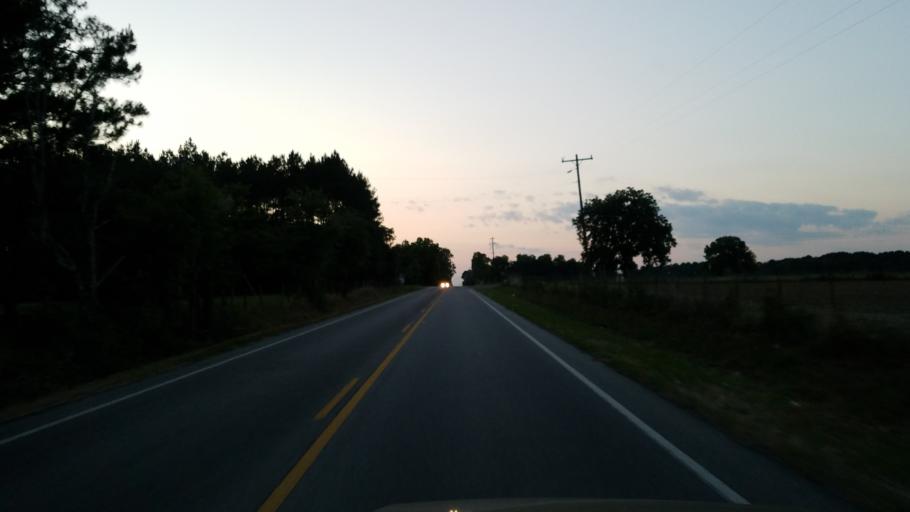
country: US
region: Georgia
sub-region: Tift County
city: Tifton
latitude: 31.5683
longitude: -83.5646
